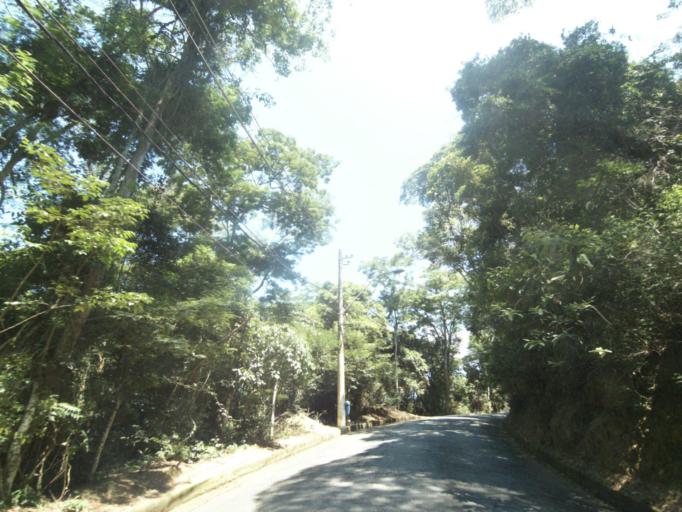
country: BR
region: Rio de Janeiro
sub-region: Niteroi
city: Niteroi
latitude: -22.9275
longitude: -43.0840
